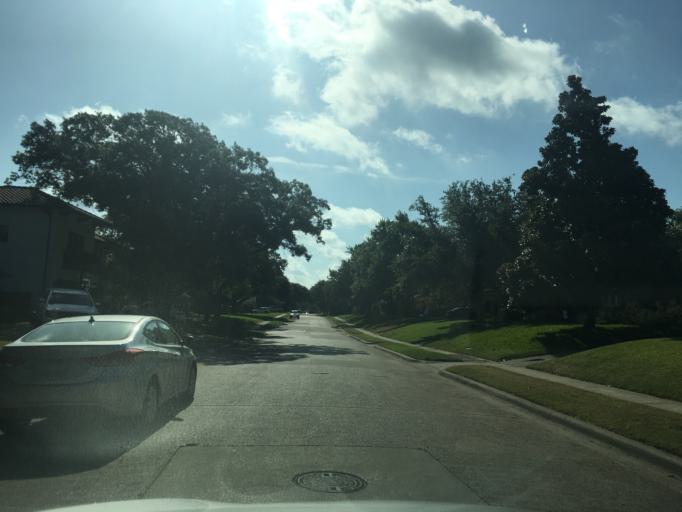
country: US
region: Texas
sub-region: Dallas County
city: Highland Park
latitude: 32.8352
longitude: -96.7483
